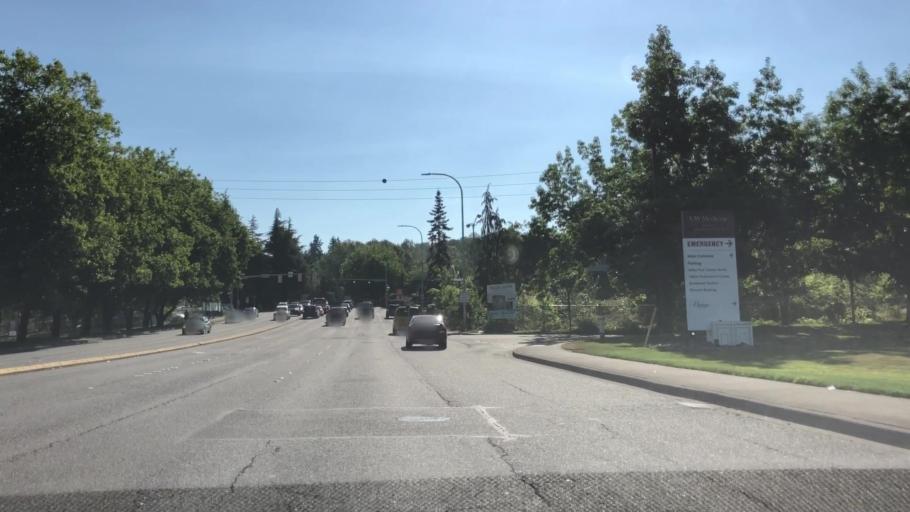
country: US
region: Washington
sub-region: King County
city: Renton
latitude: 47.4411
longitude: -122.2150
